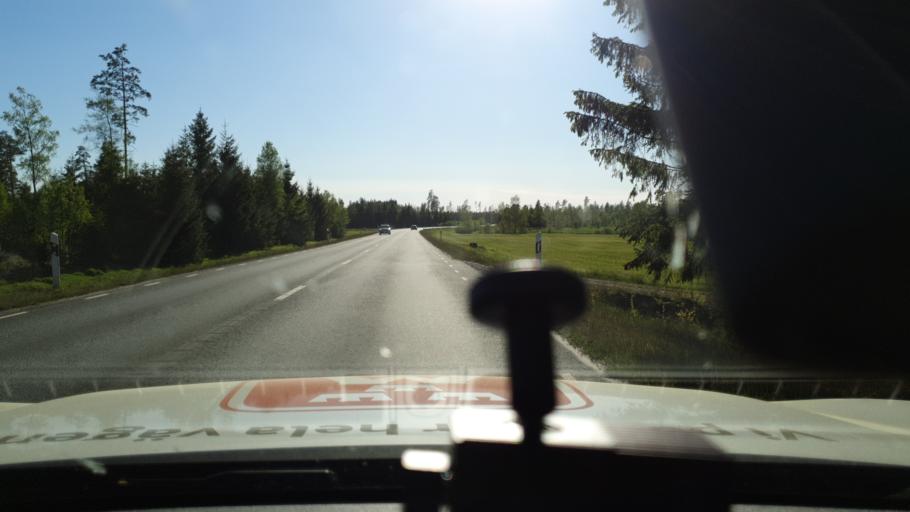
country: SE
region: Joenkoeping
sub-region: Savsjo Kommun
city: Saevsjoe
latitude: 57.3920
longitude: 14.7377
